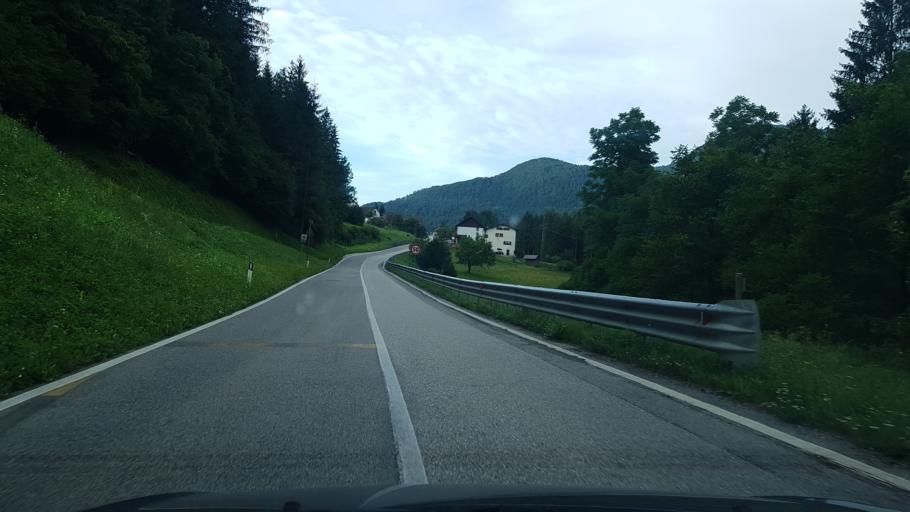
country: IT
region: Friuli Venezia Giulia
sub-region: Provincia di Udine
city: Ovaro
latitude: 46.4956
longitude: 12.8665
